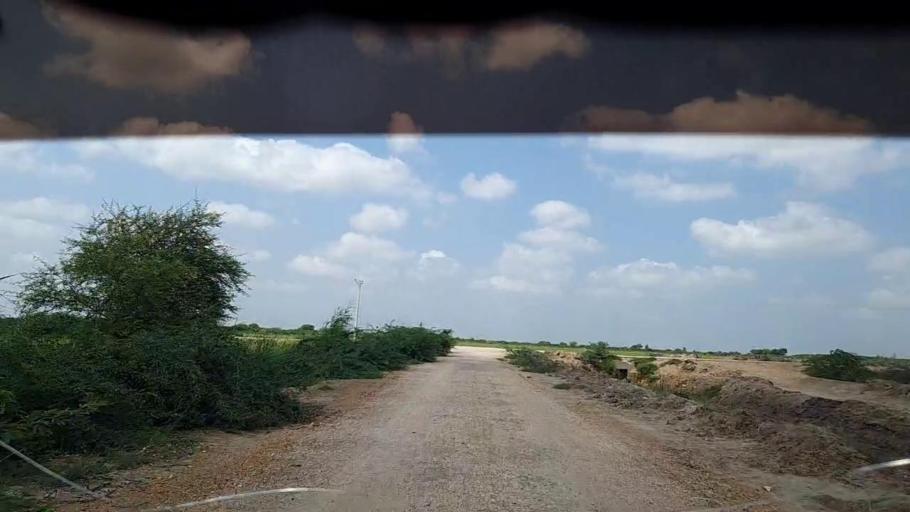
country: PK
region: Sindh
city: Kadhan
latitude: 24.5954
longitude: 68.9633
